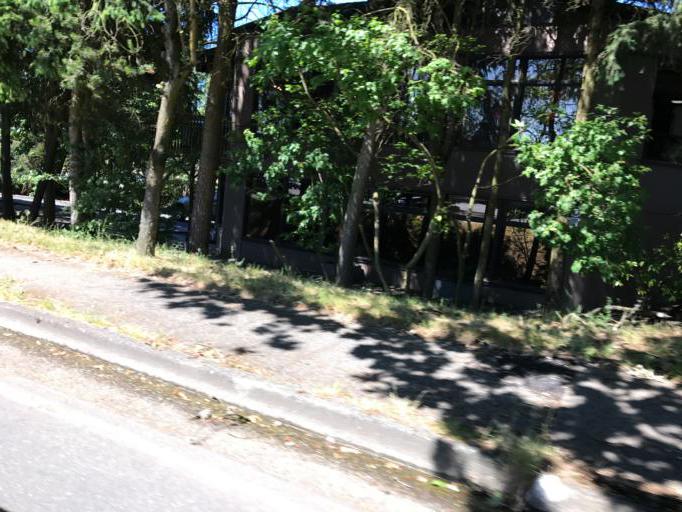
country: US
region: Washington
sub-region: King County
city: Bellevue
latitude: 47.6279
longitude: -122.1644
